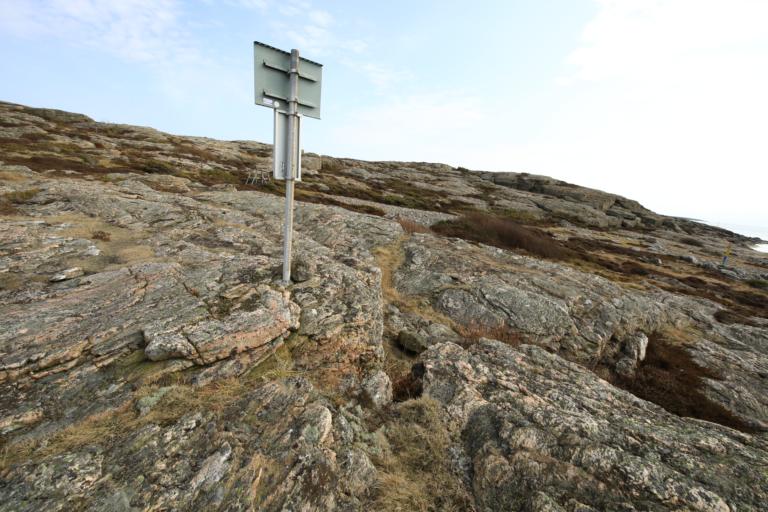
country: SE
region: Halland
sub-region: Kungsbacka Kommun
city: Frillesas
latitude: 57.2531
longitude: 12.0910
